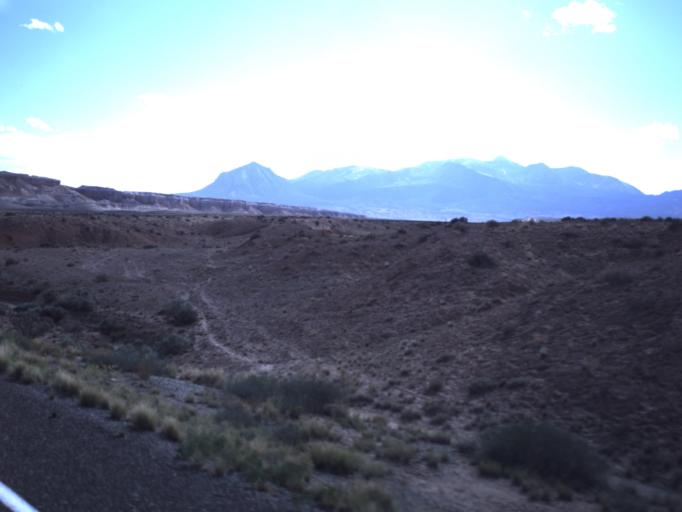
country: US
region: Utah
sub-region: Emery County
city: Ferron
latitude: 38.2986
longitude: -110.6683
